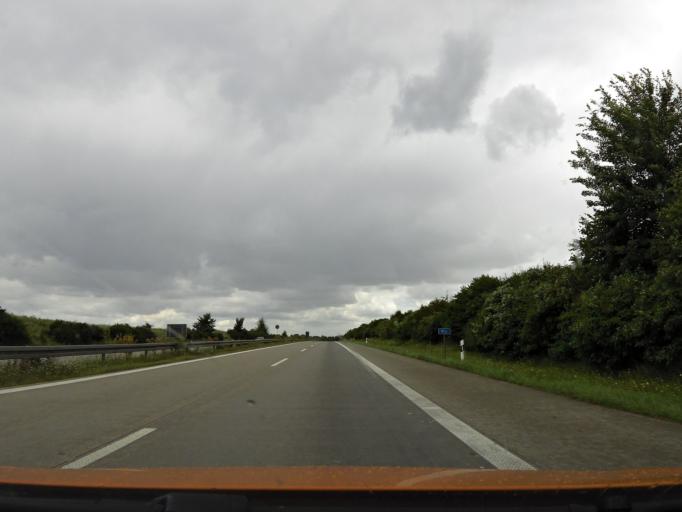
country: DE
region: Mecklenburg-Vorpommern
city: Penkun
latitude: 53.2955
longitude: 14.1397
